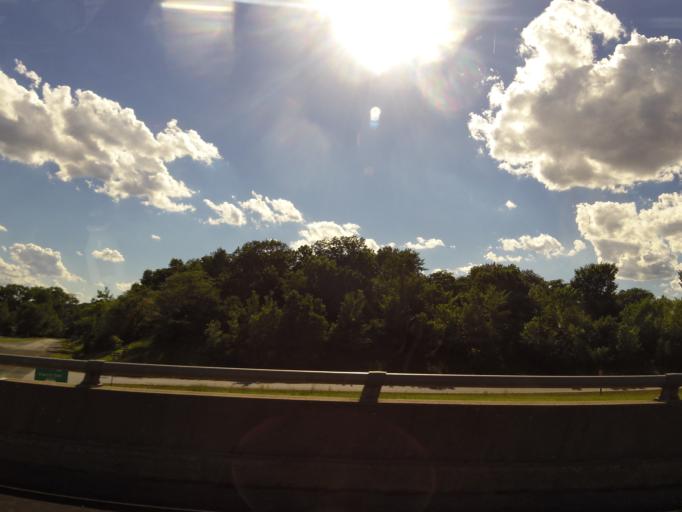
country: US
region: Illinois
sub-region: Adams County
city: Quincy
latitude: 40.0119
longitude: -91.5266
